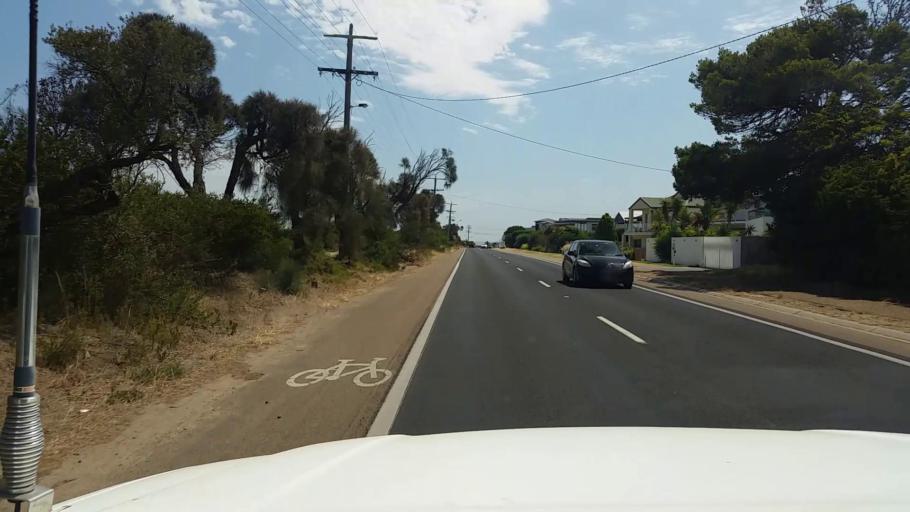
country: AU
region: Victoria
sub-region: Mornington Peninsula
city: Mornington
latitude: -38.2324
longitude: 145.0271
